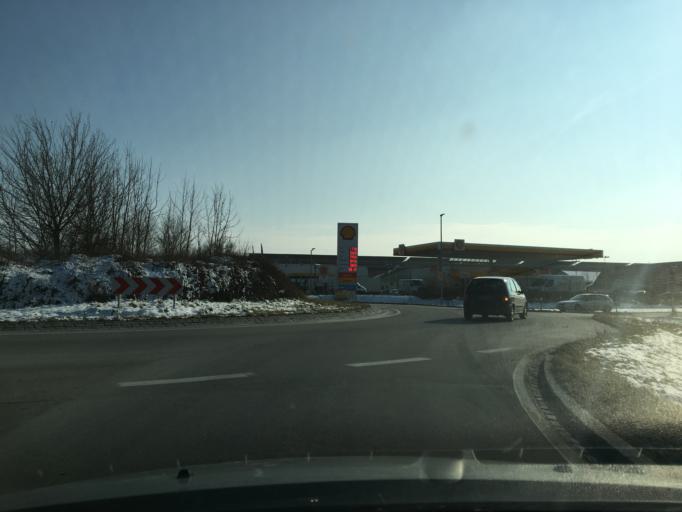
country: DE
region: Bavaria
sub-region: Lower Bavaria
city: Frontenhausen
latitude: 48.5508
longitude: 12.5451
